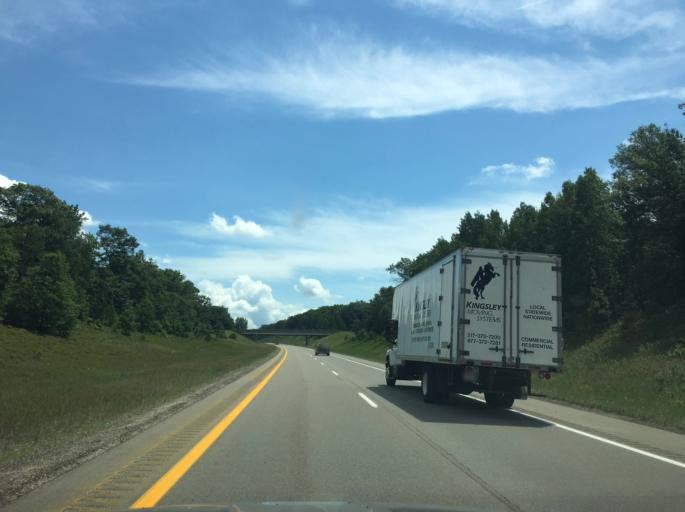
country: US
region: Michigan
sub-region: Roscommon County
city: Roscommon
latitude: 44.4961
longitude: -84.6500
